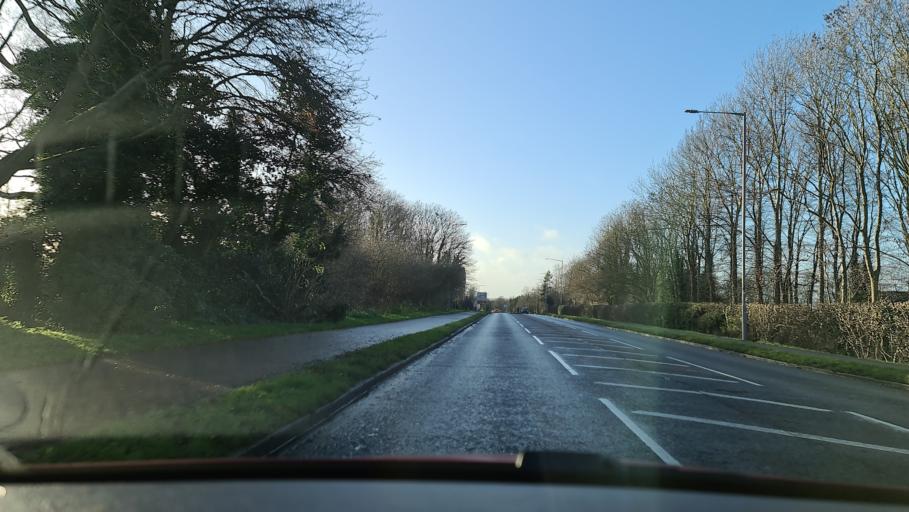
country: GB
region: England
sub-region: Milton Keynes
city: Stony Stratford
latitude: 52.0619
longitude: -0.8251
